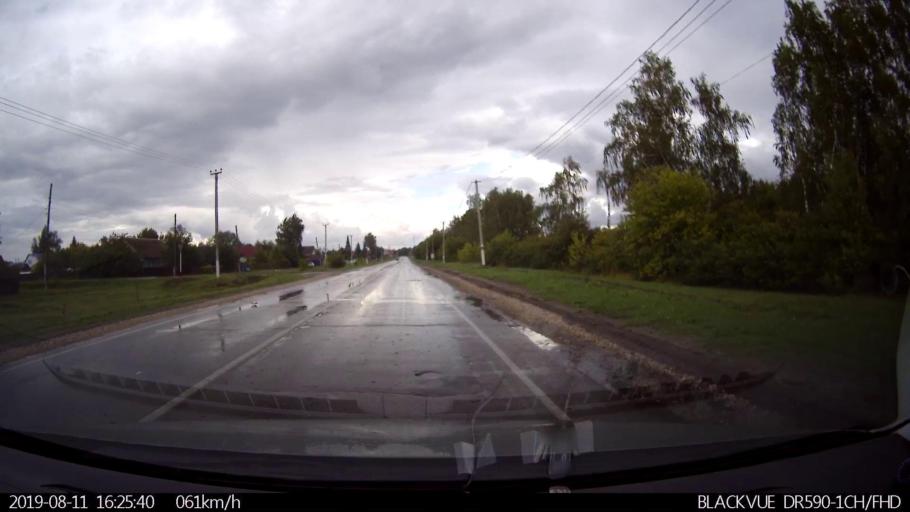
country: RU
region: Ulyanovsk
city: Mayna
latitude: 54.1067
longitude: 47.6072
